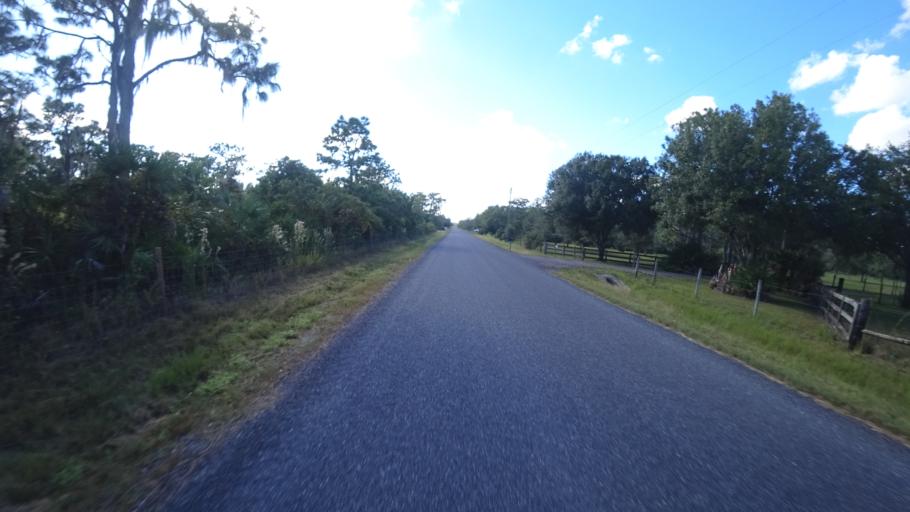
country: US
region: Florida
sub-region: Sarasota County
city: Fruitville
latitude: 27.4053
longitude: -82.2941
